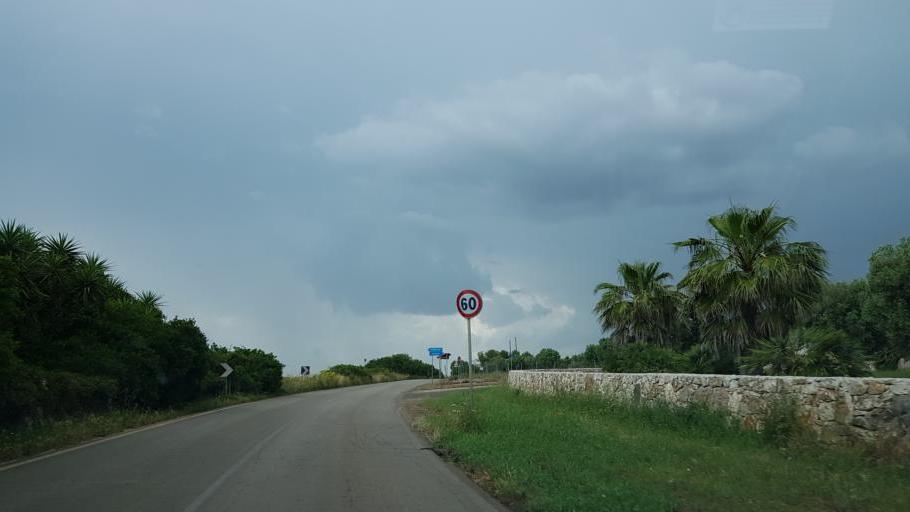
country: IT
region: Apulia
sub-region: Provincia di Lecce
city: Porto Cesareo
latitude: 40.3255
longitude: 17.8538
